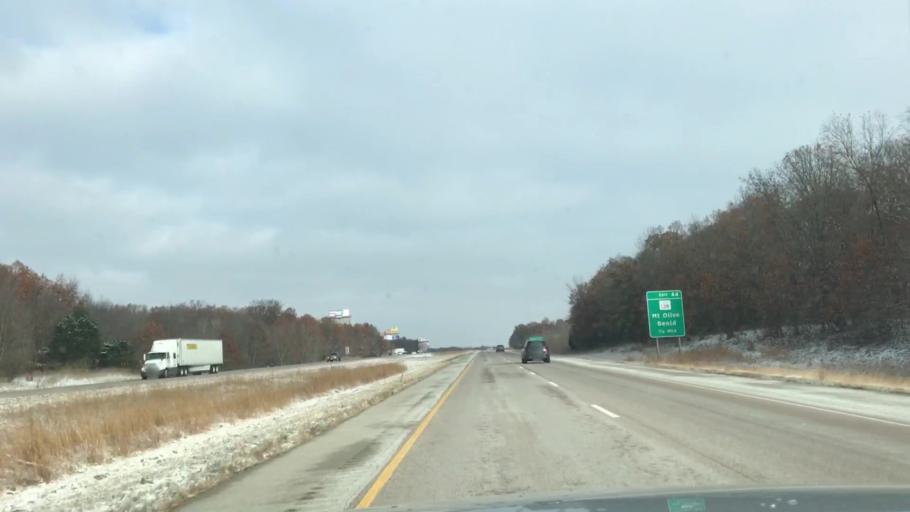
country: US
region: Illinois
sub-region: Macoupin County
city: Mount Olive
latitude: 39.0604
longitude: -89.7556
